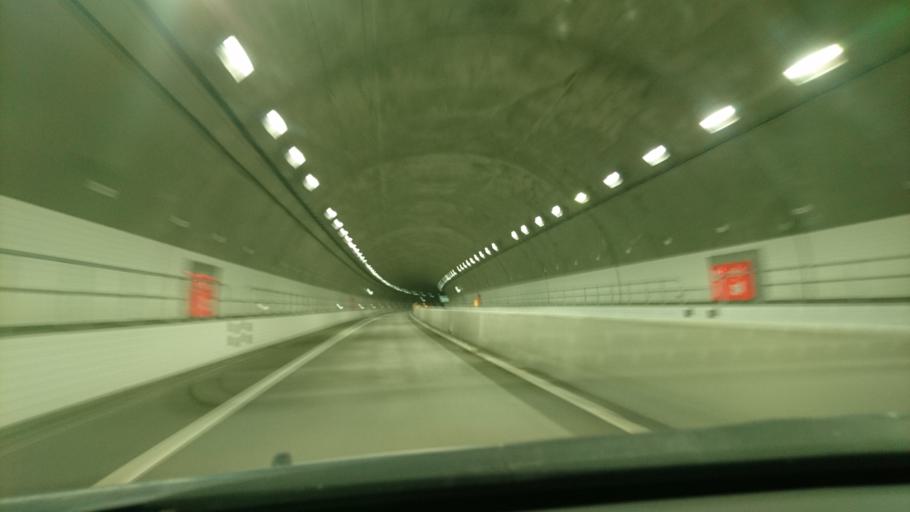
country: JP
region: Iwate
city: Miyako
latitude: 39.8057
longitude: 141.9552
